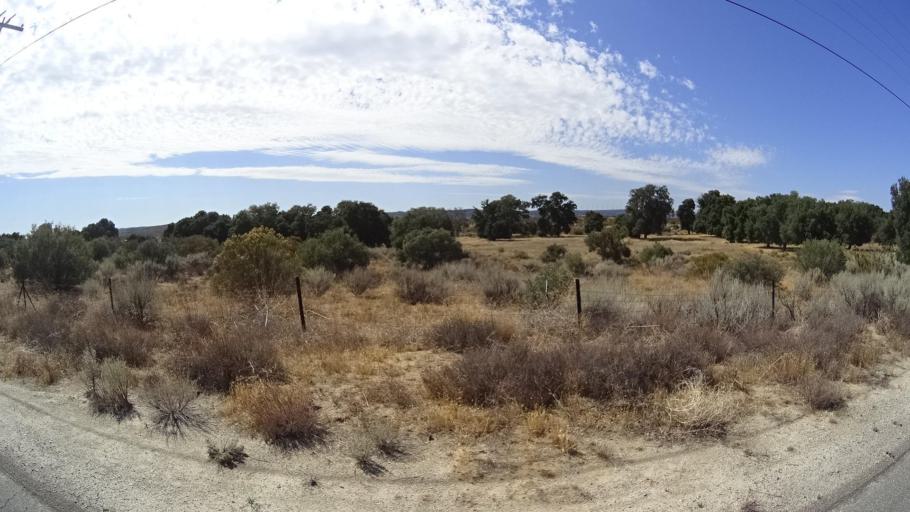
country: MX
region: Baja California
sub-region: Tecate
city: Cereso del Hongo
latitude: 32.6907
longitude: -116.2598
